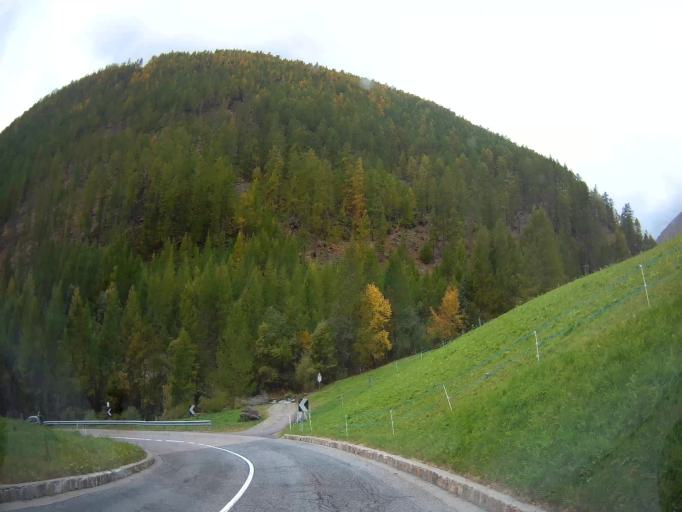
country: IT
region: Trentino-Alto Adige
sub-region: Bolzano
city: Senales
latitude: 46.7285
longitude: 10.8545
